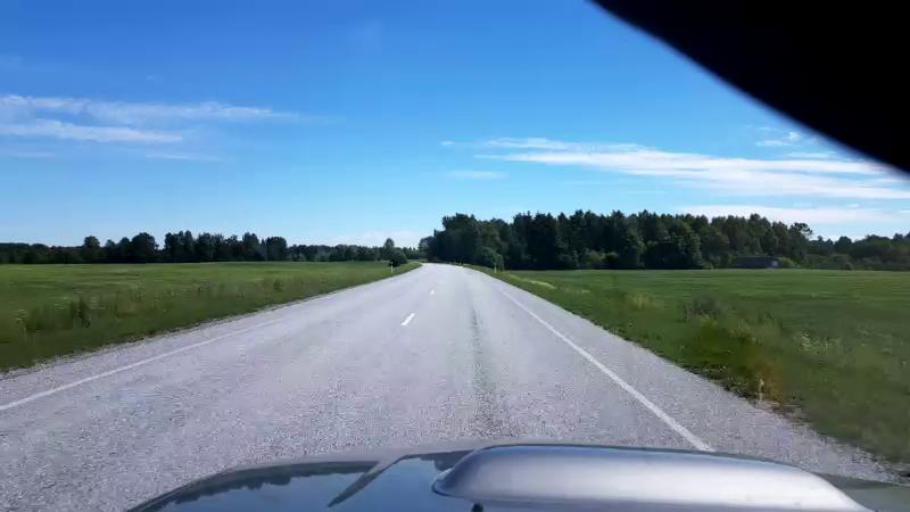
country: EE
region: Laeaene-Virumaa
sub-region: Rakke vald
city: Rakke
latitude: 58.9463
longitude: 26.1864
